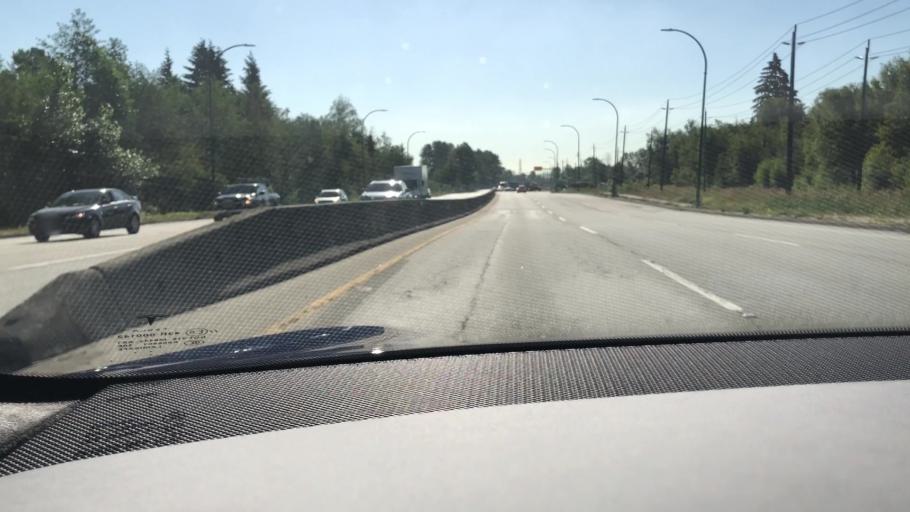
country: CA
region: British Columbia
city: New Westminster
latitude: 49.1972
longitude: -122.9737
